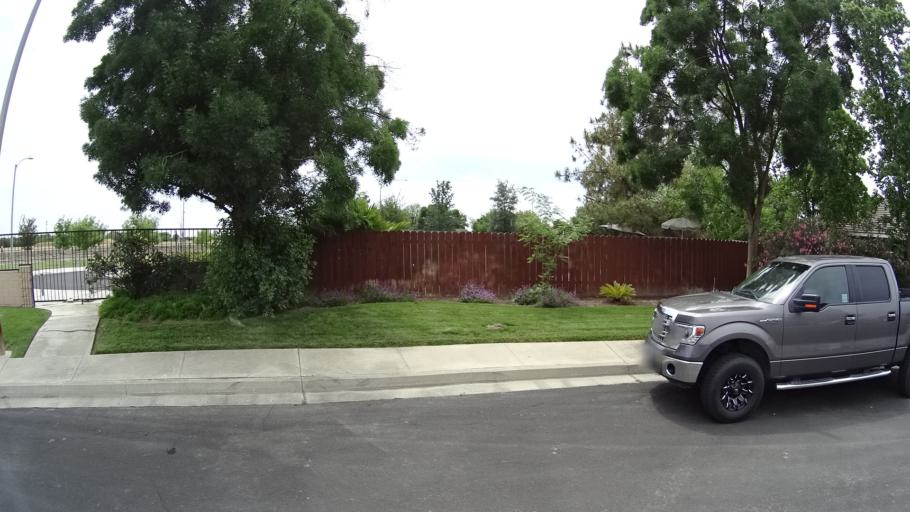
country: US
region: California
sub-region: Kings County
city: Lucerne
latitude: 36.3668
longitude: -119.6372
